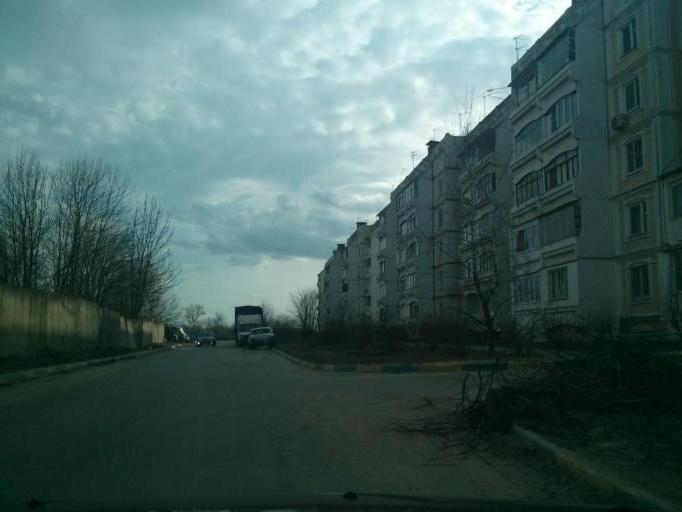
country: RU
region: Nizjnij Novgorod
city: Nizhniy Novgorod
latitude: 56.2621
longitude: 44.0094
